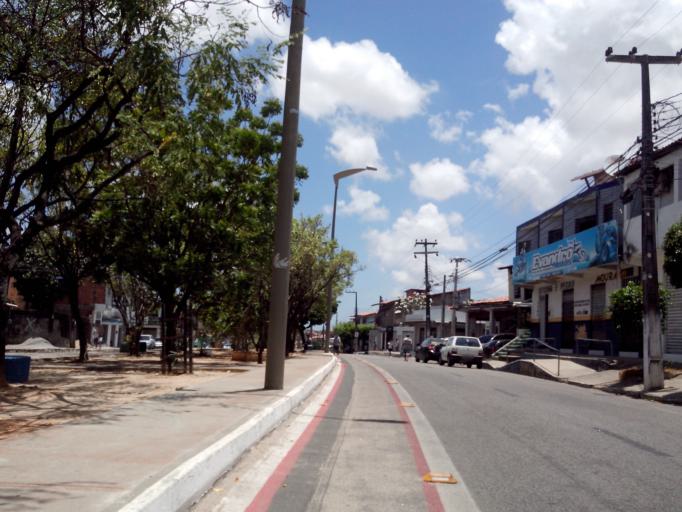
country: BR
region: Ceara
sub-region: Caucaia
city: Caucaia
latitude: -3.7710
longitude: -38.6025
